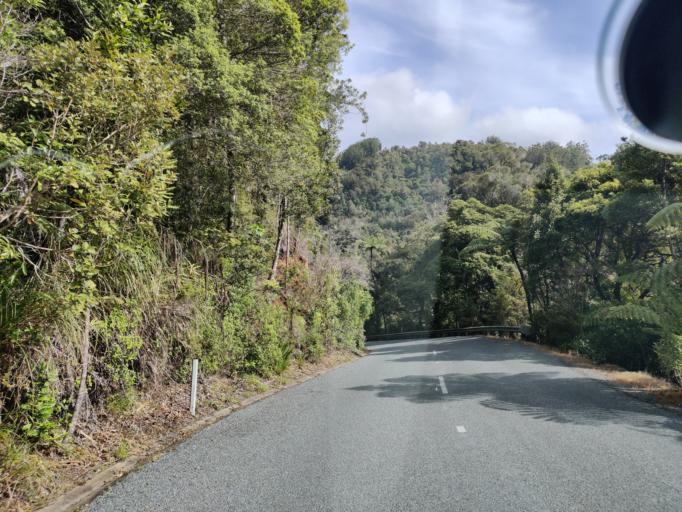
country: NZ
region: Northland
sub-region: Kaipara District
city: Dargaville
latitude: -35.6511
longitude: 173.5664
